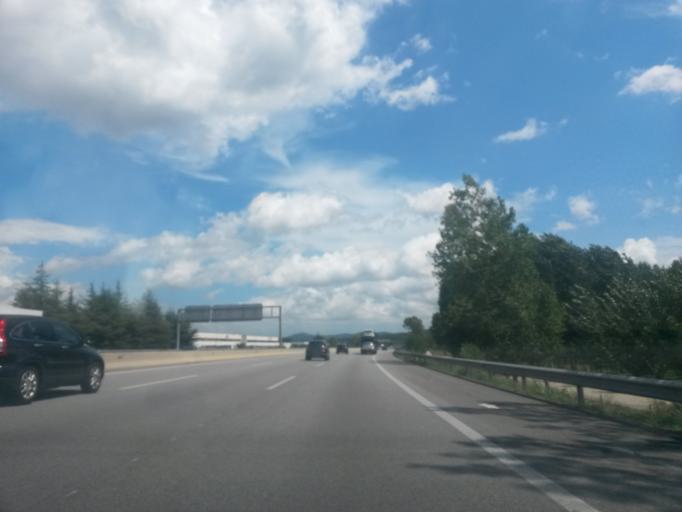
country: ES
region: Catalonia
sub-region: Provincia de Girona
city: Hostalric
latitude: 41.7420
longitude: 2.6515
